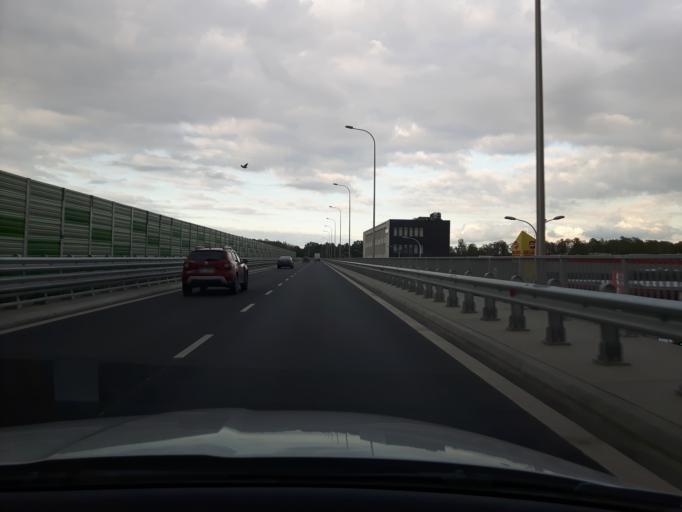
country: PL
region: Masovian Voivodeship
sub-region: Warszawa
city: Rembertow
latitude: 52.2415
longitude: 21.1356
